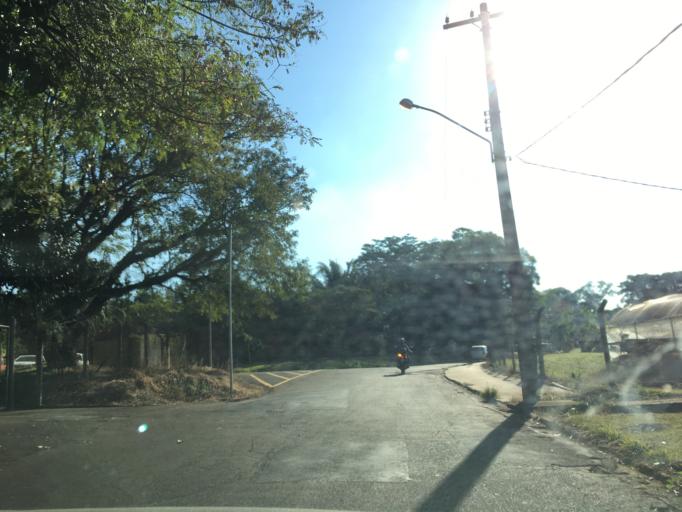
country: BR
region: Sao Paulo
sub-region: Piracicaba
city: Piracicaba
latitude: -22.7125
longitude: -47.6289
